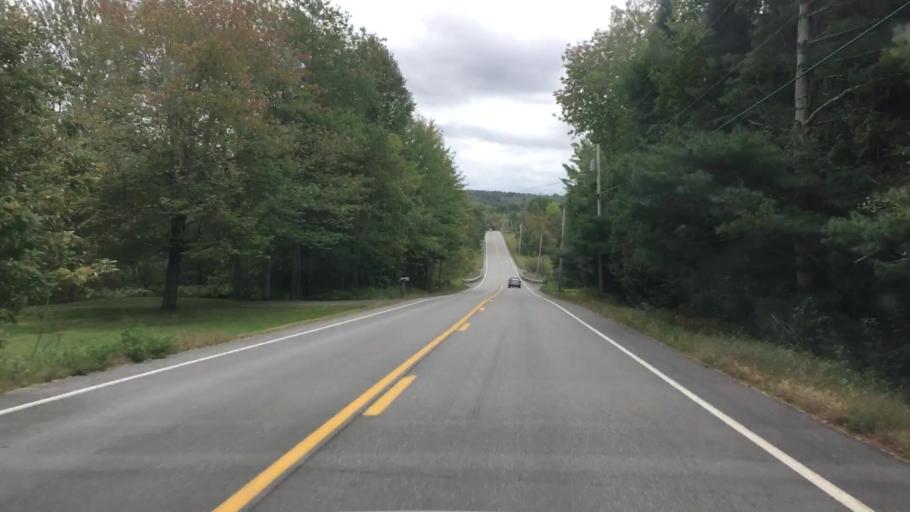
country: US
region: Maine
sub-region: Penobscot County
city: Hermon
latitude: 44.7523
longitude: -68.9710
